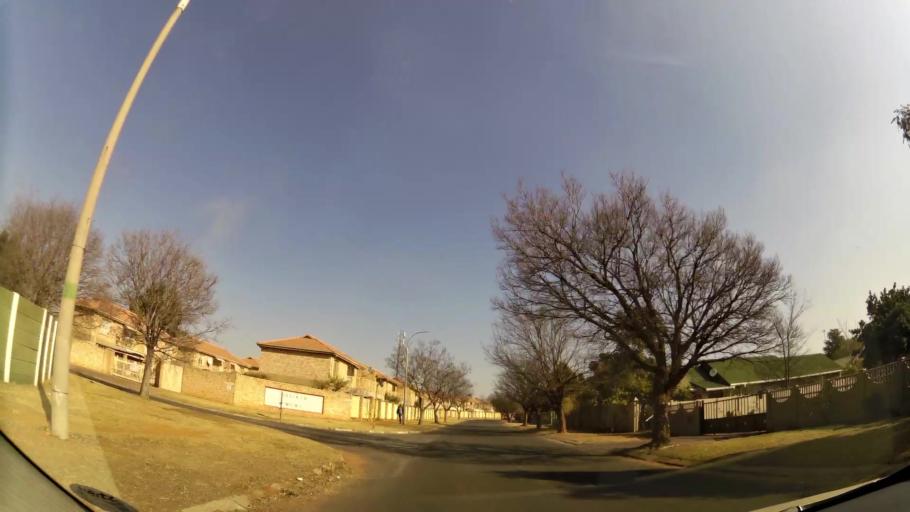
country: ZA
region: Gauteng
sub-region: West Rand District Municipality
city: Randfontein
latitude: -26.1809
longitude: 27.6831
